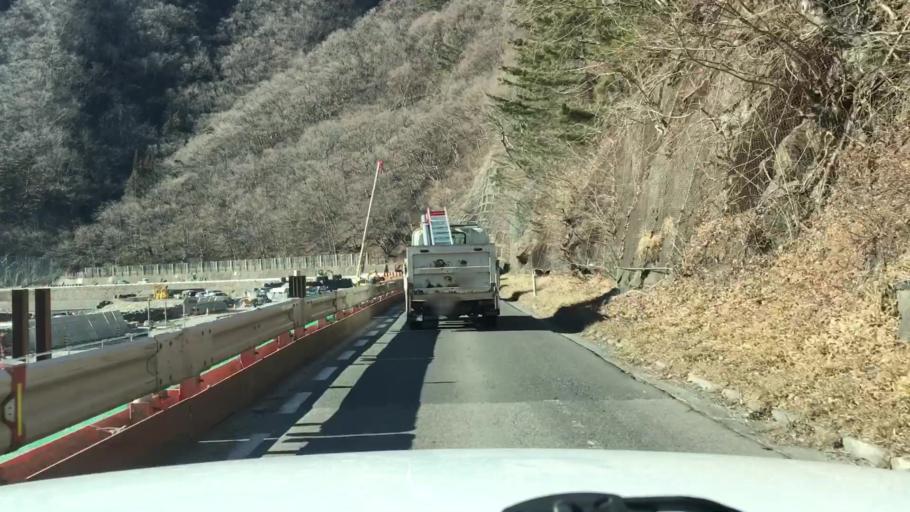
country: JP
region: Iwate
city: Miyako
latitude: 39.6277
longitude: 141.8132
